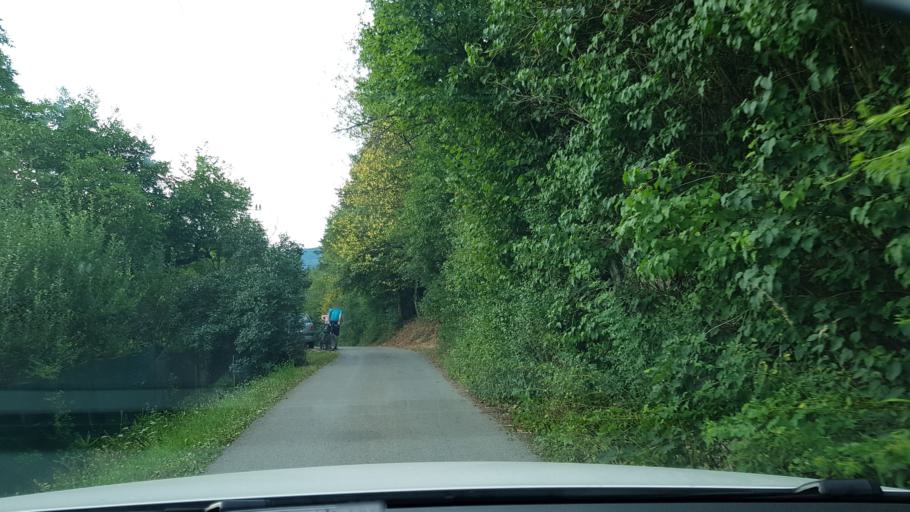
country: SK
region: Trenciansky
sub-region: Okres Povazska Bystrica
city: Povazska Bystrica
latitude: 49.1116
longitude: 18.4561
